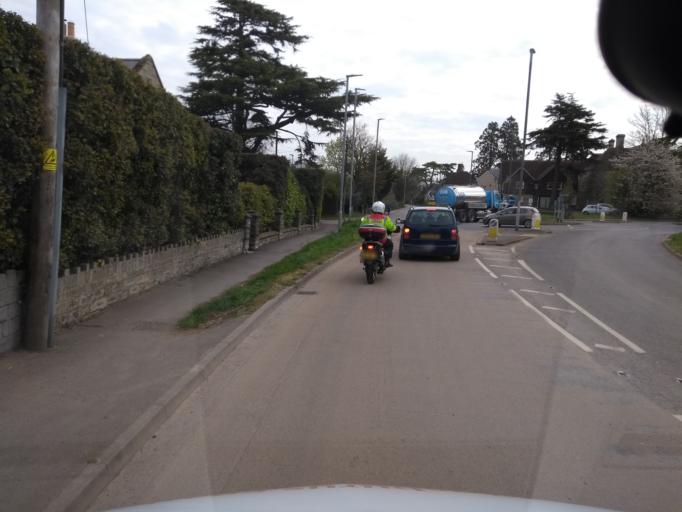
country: GB
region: England
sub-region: Somerset
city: Langport
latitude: 51.0445
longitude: -2.8192
